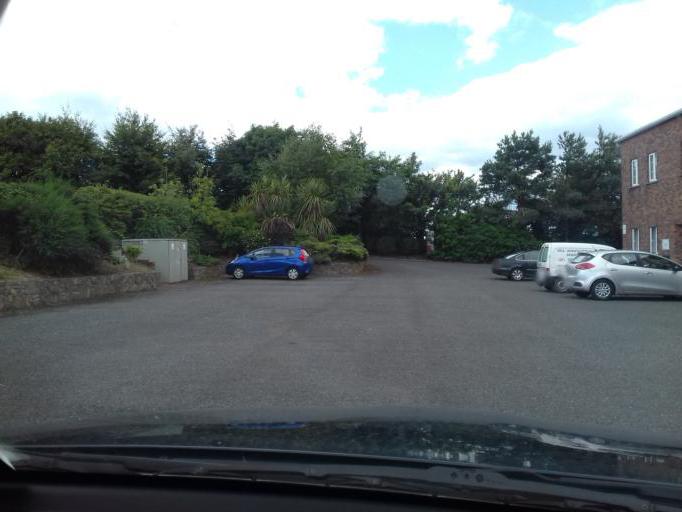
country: IE
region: Munster
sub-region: Waterford
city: Tra Mhor
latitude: 52.1768
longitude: -7.2508
